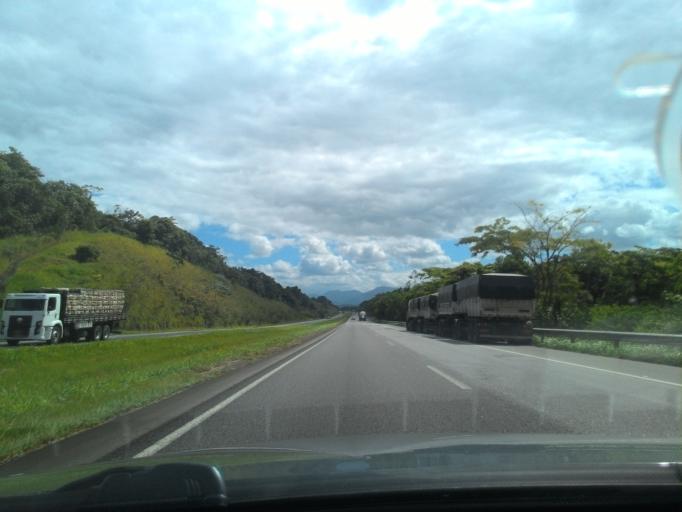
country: BR
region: Sao Paulo
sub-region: Jacupiranga
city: Jacupiranga
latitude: -24.6580
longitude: -47.9668
